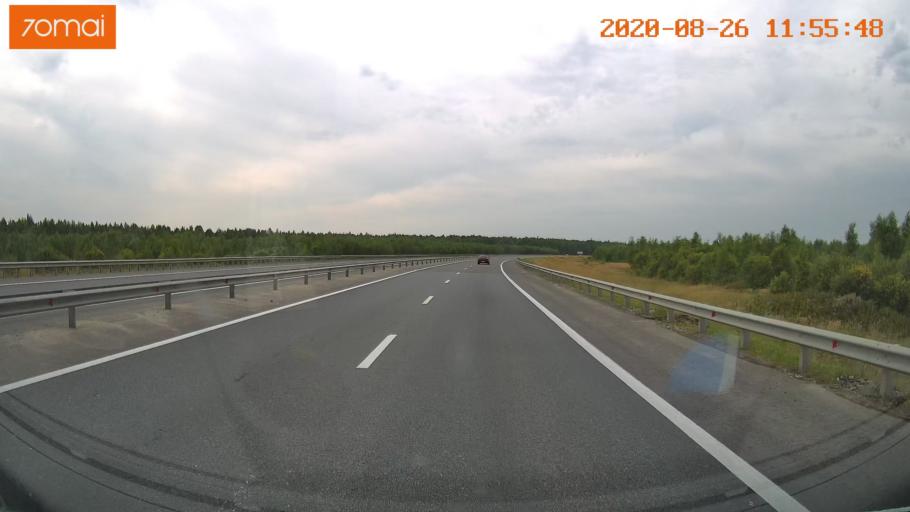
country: RU
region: Rjazan
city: Kiritsy
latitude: 54.2686
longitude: 40.3899
